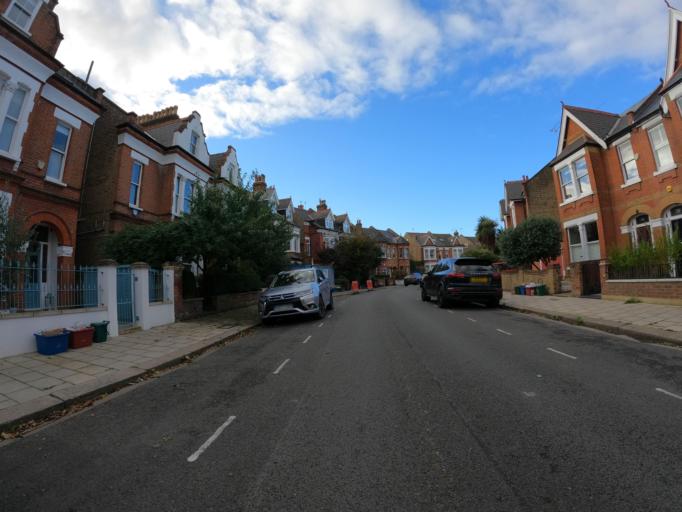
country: GB
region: England
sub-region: Greater London
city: Acton
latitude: 51.4854
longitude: -0.2738
